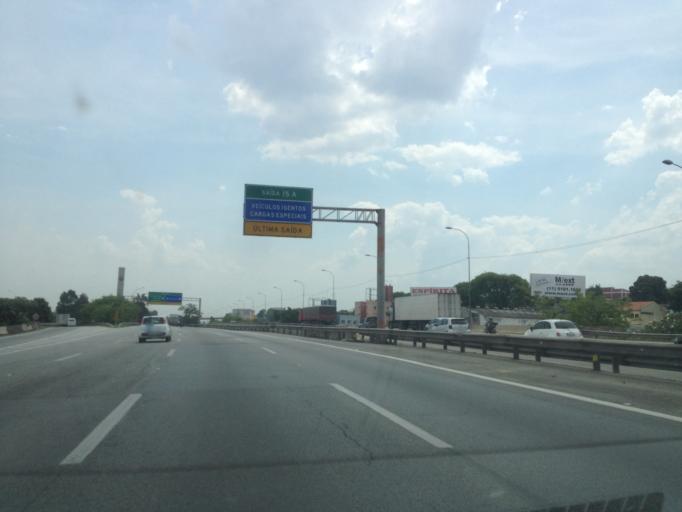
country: BR
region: Sao Paulo
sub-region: Osasco
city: Osasco
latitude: -23.5204
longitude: -46.7686
